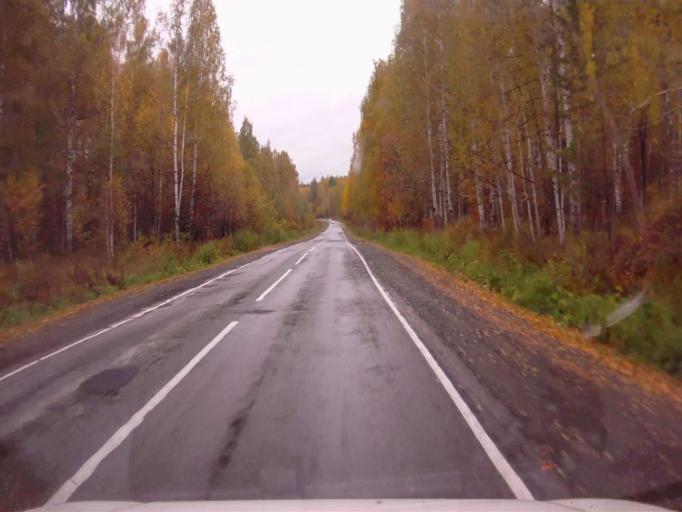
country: RU
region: Chelyabinsk
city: Nizhniy Ufaley
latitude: 56.0539
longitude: 59.9550
